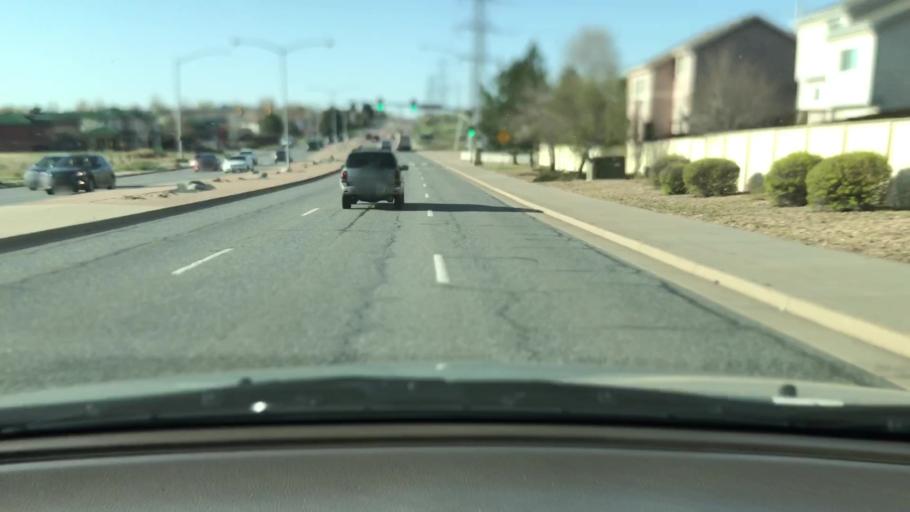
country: US
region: Colorado
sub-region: Adams County
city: Aurora
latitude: 39.6663
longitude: -104.7723
